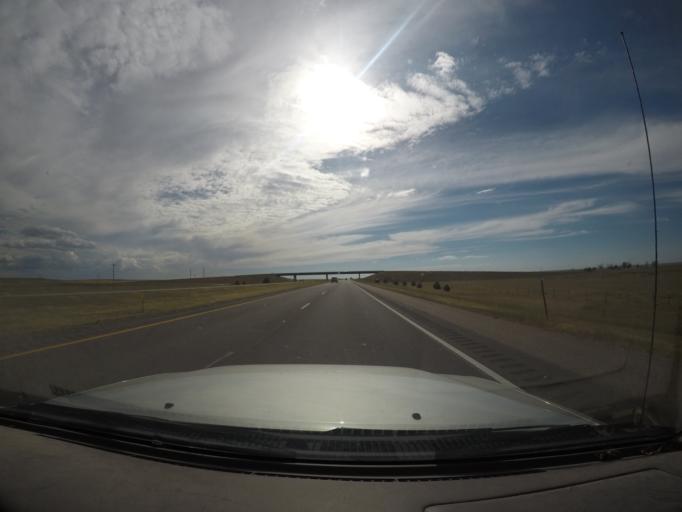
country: US
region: Nebraska
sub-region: Kimball County
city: Kimball
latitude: 41.1919
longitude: -103.7945
